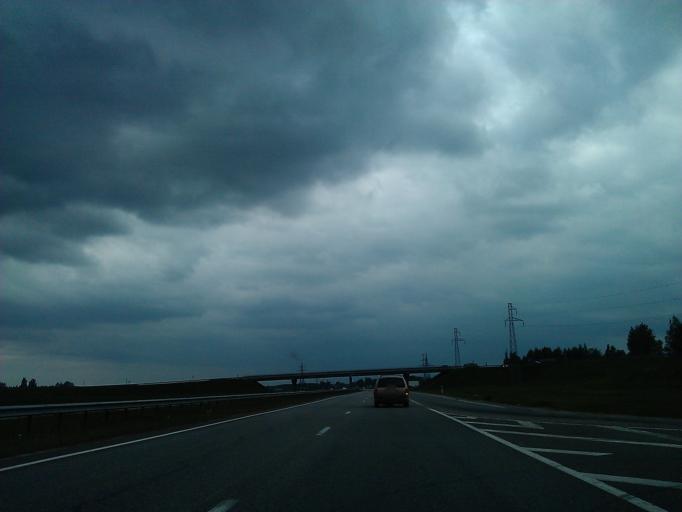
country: LV
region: Marupe
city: Marupe
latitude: 56.8362
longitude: 24.0425
